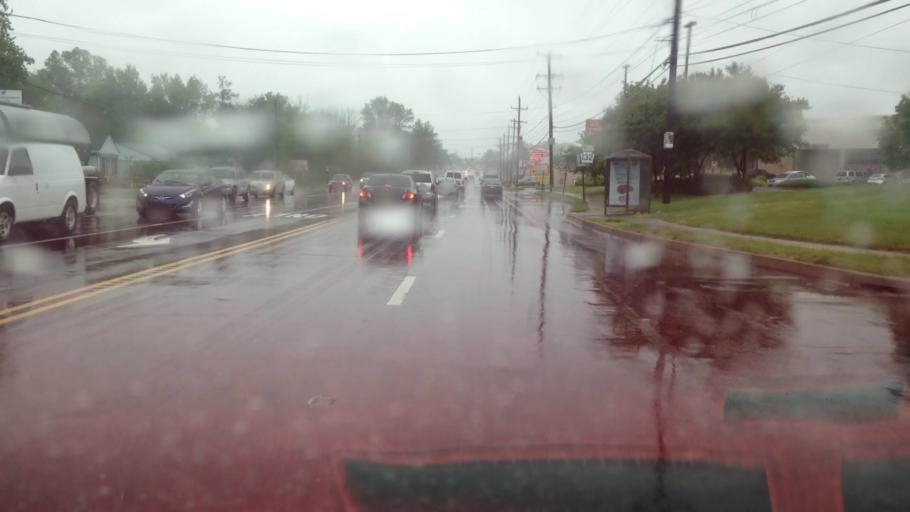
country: US
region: Pennsylvania
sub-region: Bucks County
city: Eddington
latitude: 40.1051
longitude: -74.9507
